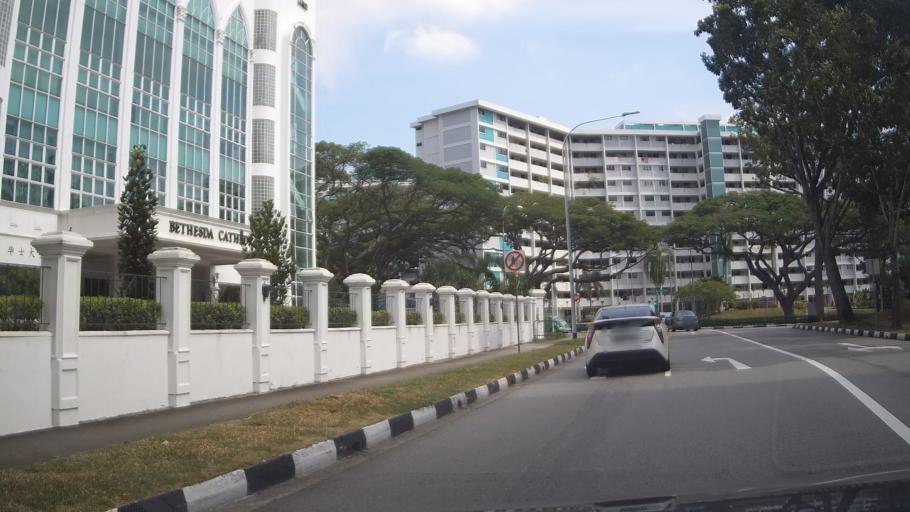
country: SG
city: Singapore
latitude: 1.3287
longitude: 103.9238
